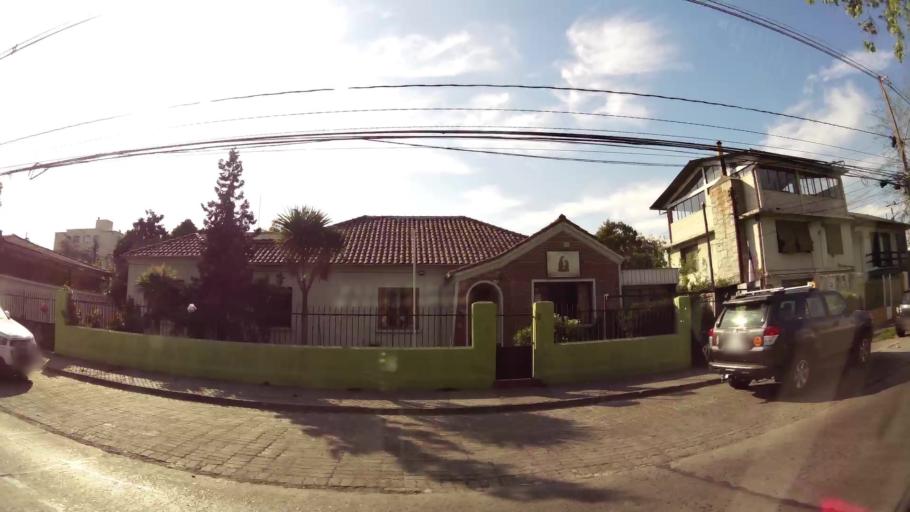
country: CL
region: Santiago Metropolitan
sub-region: Provincia de Maipo
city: San Bernardo
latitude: -33.6017
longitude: -70.7027
